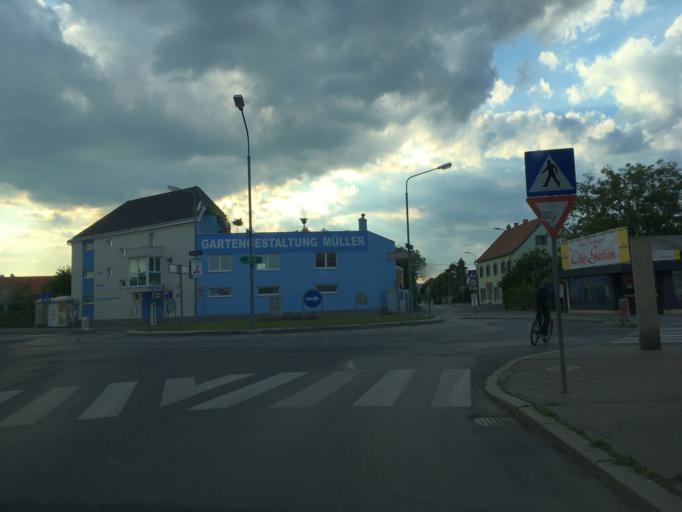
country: AT
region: Lower Austria
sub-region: Politischer Bezirk Wien-Umgebung
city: Gerasdorf bei Wien
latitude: 48.2879
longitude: 16.4487
